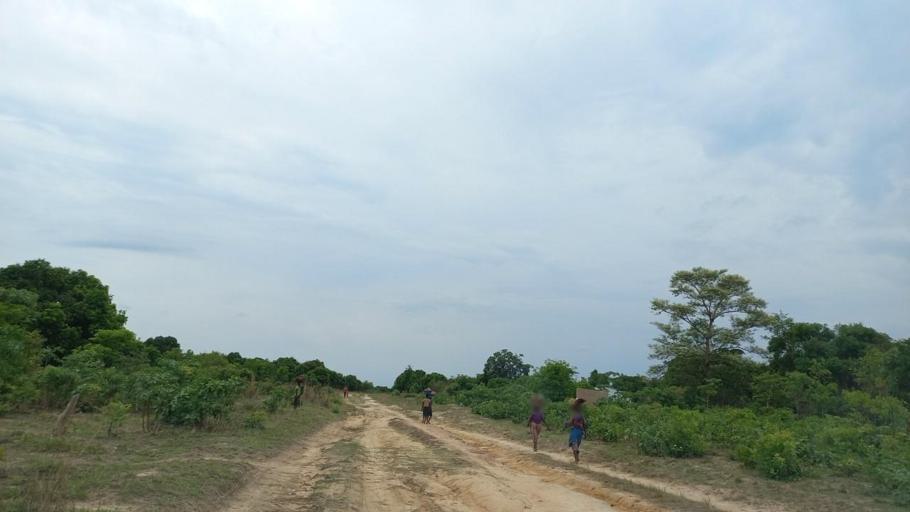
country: ZM
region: North-Western
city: Kalengwa
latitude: -13.6403
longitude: 24.9803
